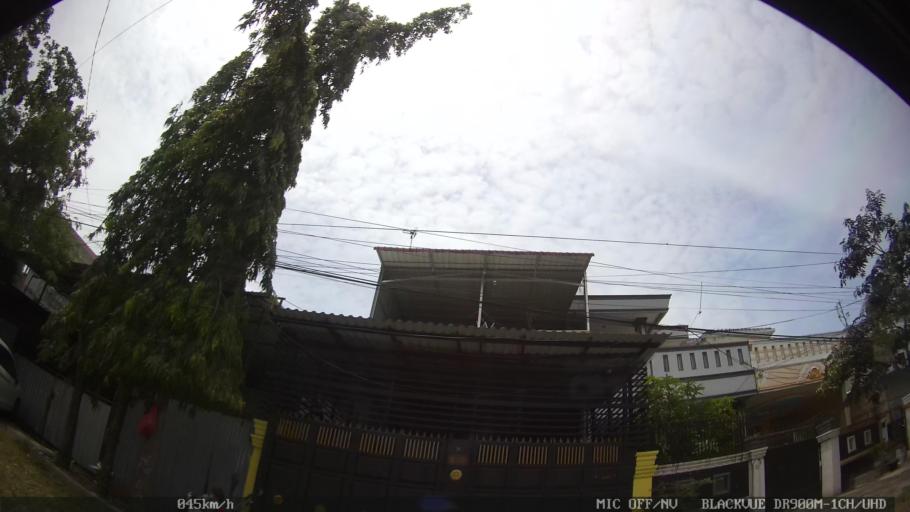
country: ID
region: North Sumatra
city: Sunggal
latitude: 3.5551
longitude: 98.6418
